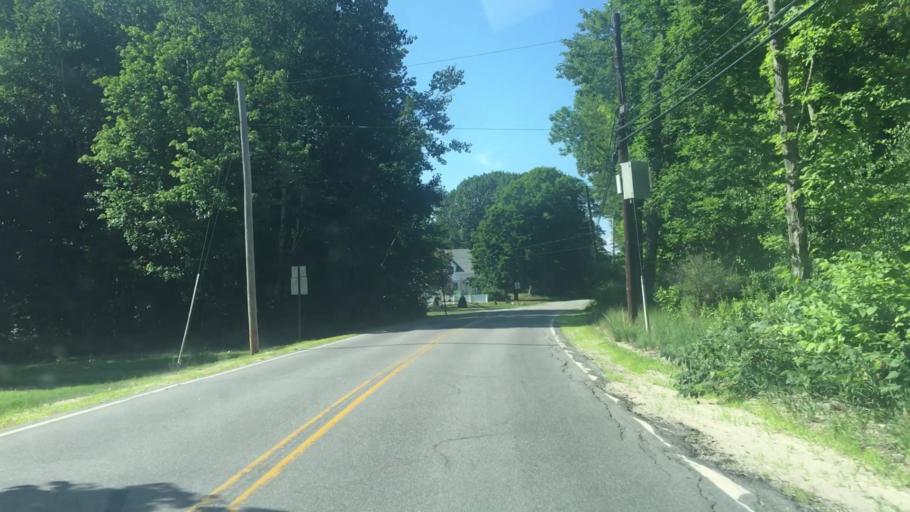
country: US
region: Maine
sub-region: York County
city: Buxton
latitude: 43.6138
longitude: -70.5415
